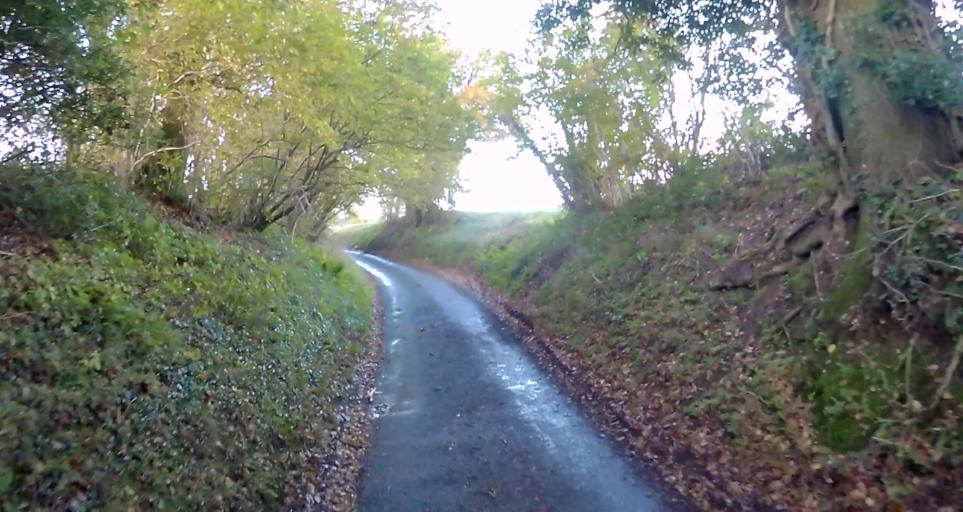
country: GB
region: England
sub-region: Hampshire
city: Basingstoke
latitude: 51.2104
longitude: -1.0886
